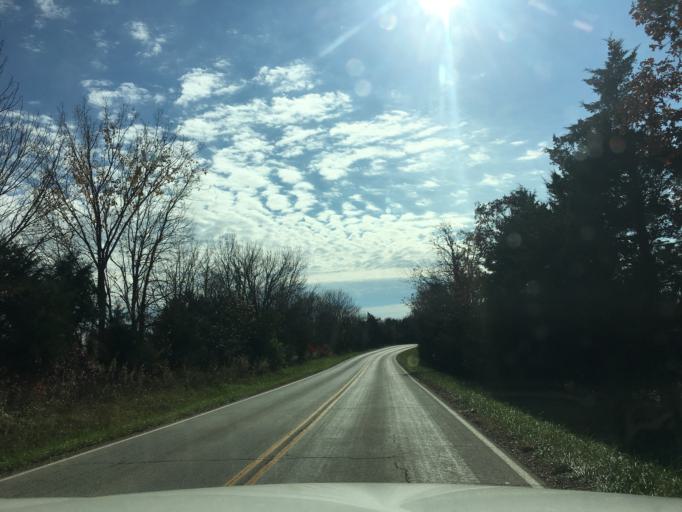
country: US
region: Missouri
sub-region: Osage County
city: Linn
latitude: 38.4524
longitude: -91.8370
